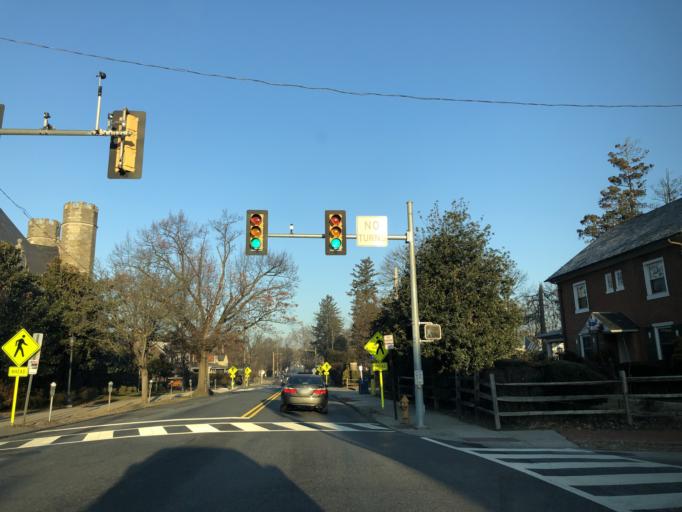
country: US
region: Pennsylvania
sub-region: Chester County
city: West Chester
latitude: 39.9531
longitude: -75.5973
